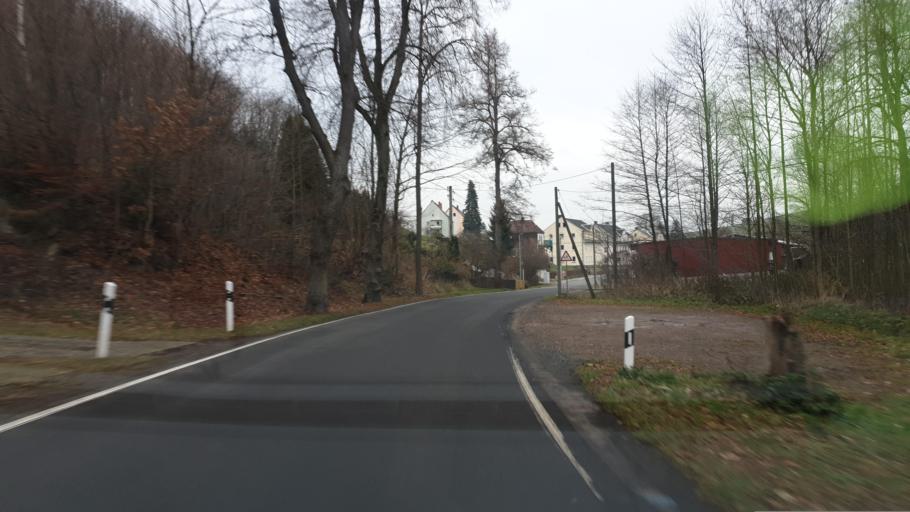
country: DE
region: Saxony
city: Mulda
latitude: 50.8051
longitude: 13.4065
